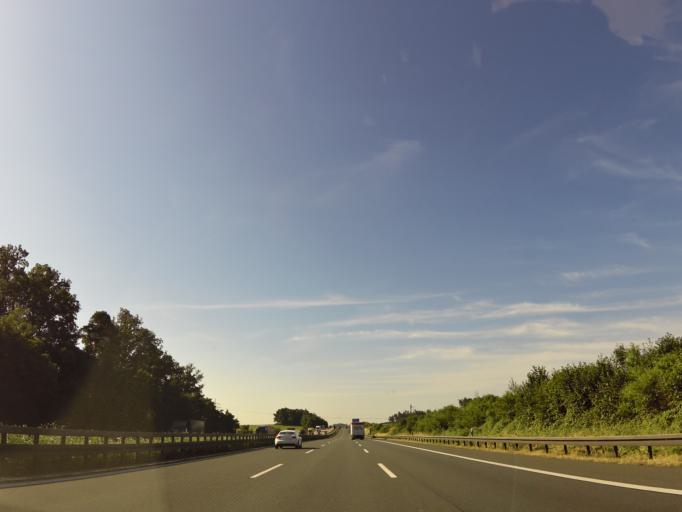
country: DE
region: Bavaria
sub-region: Regierungsbezirk Mittelfranken
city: Allersberg
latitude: 49.2590
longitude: 11.2139
